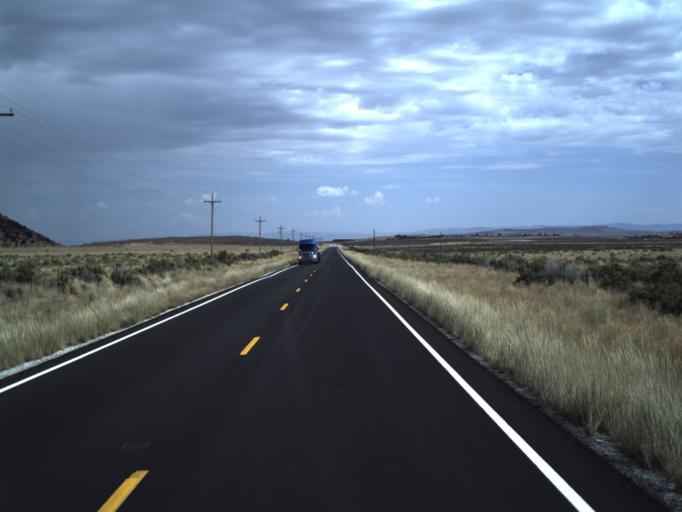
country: US
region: Idaho
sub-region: Minidoka County
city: Rupert
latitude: 41.8238
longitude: -113.1831
